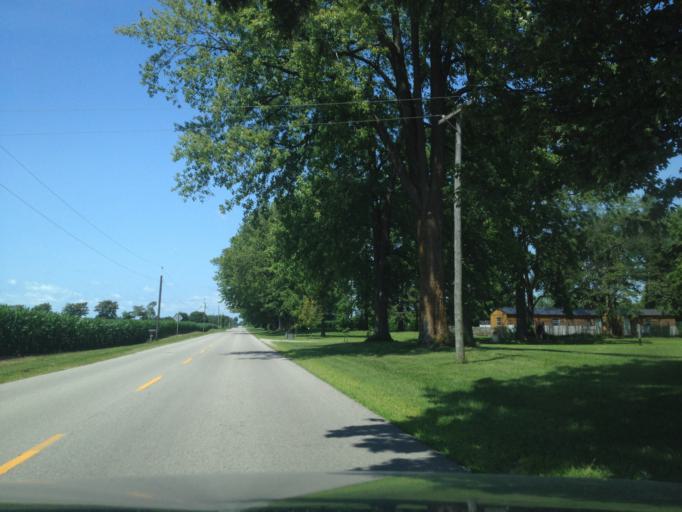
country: CA
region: Ontario
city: Aylmer
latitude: 42.6050
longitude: -80.6724
